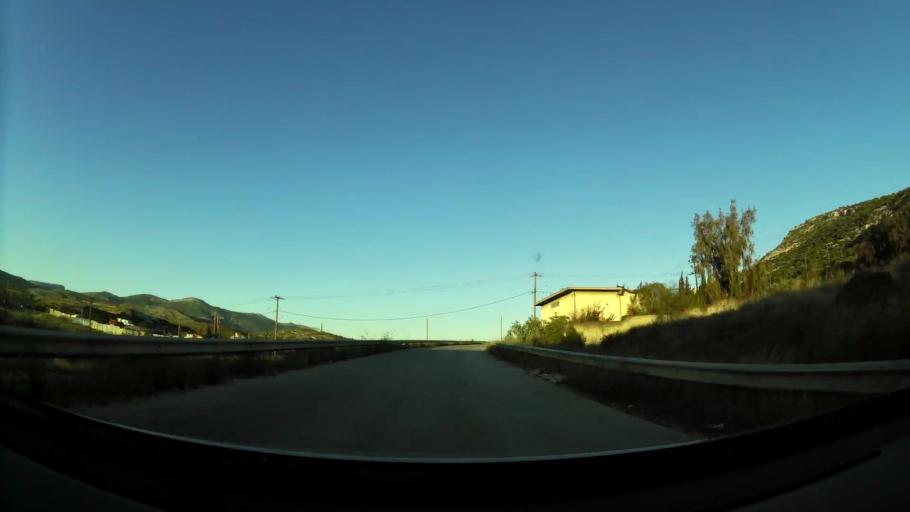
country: GR
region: Attica
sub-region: Nomarchia Athinas
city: Petroupolis
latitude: 38.0584
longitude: 23.6587
